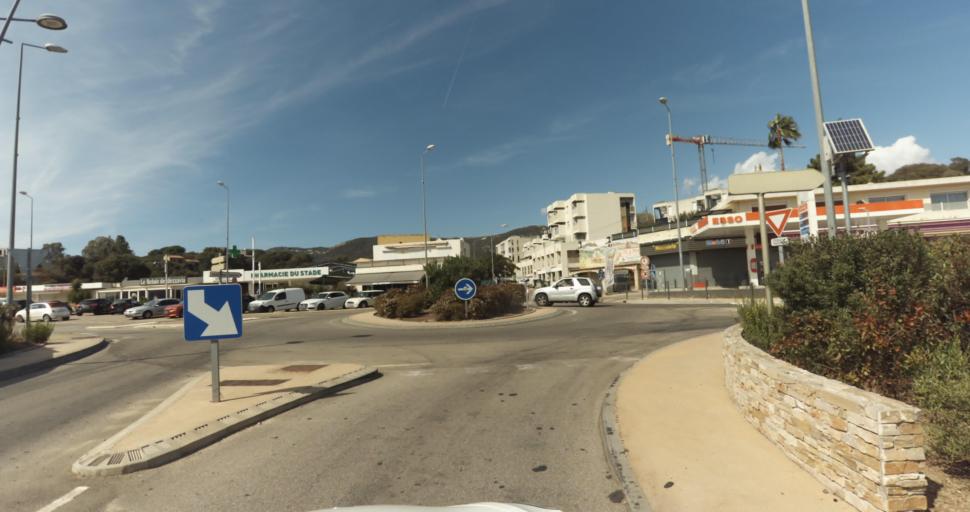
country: FR
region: Corsica
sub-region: Departement de la Corse-du-Sud
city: Afa
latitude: 41.9518
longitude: 8.7746
